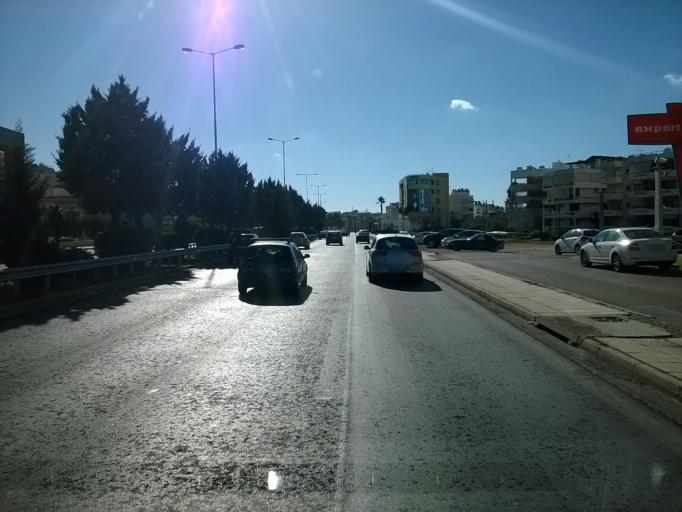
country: GR
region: Attica
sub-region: Nomarchia Athinas
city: Glyfada
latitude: 37.8637
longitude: 23.7618
